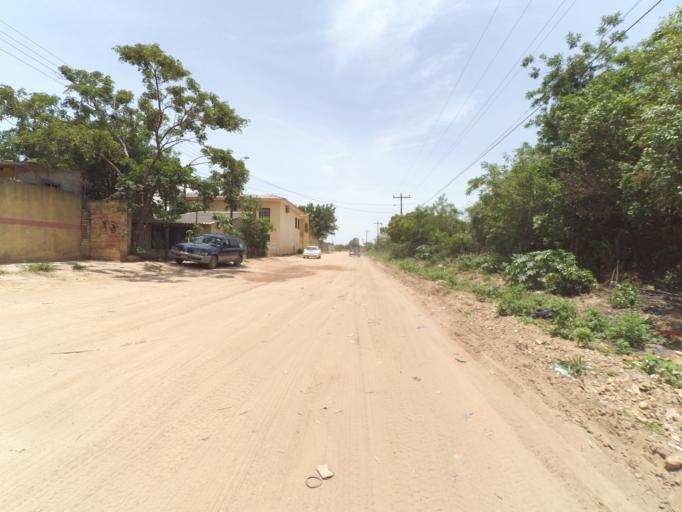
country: BO
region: Santa Cruz
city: Santa Cruz de la Sierra
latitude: -17.8233
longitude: -63.2477
